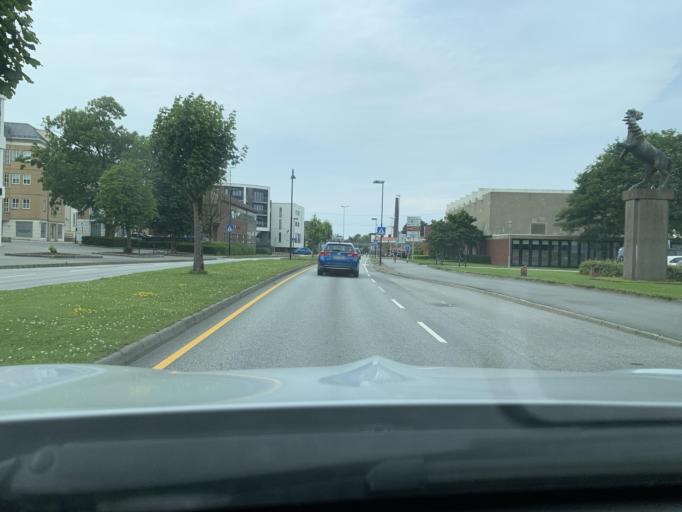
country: NO
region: Rogaland
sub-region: Time
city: Bryne
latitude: 58.7356
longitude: 5.6530
